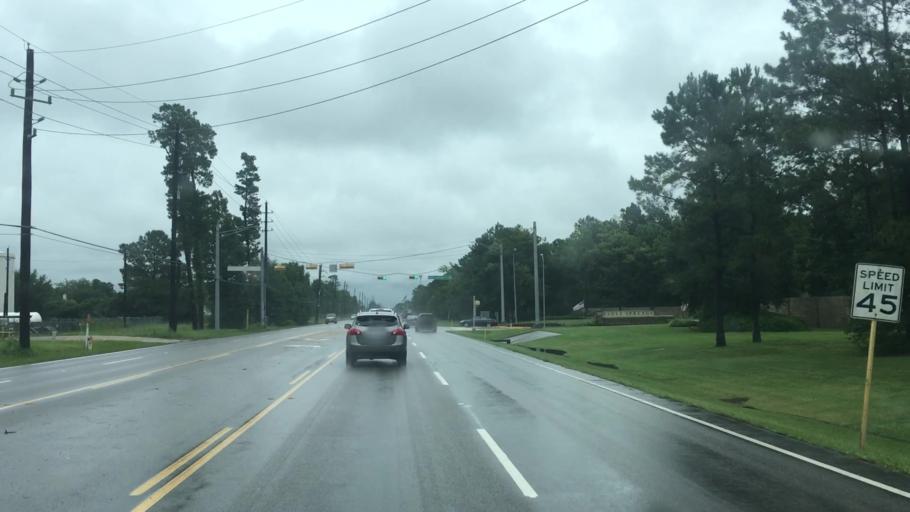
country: US
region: Texas
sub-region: Harris County
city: Atascocita
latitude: 29.9907
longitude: -95.1860
